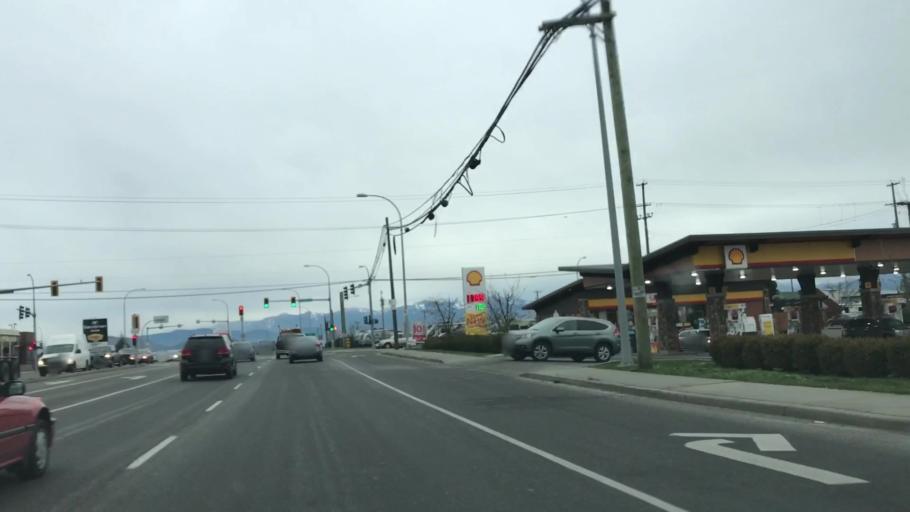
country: CA
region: British Columbia
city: Aldergrove
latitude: 49.0559
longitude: -122.3824
